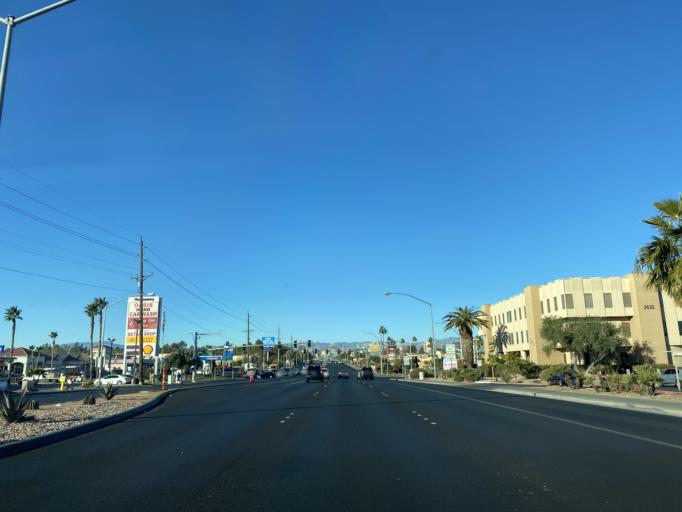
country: US
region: Nevada
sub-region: Clark County
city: Winchester
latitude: 36.1153
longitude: -115.0995
